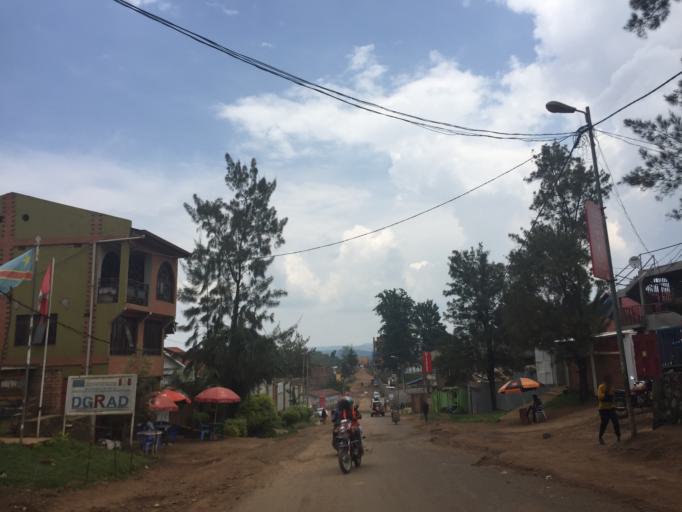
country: CD
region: South Kivu
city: Bukavu
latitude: -2.4868
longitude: 28.8575
